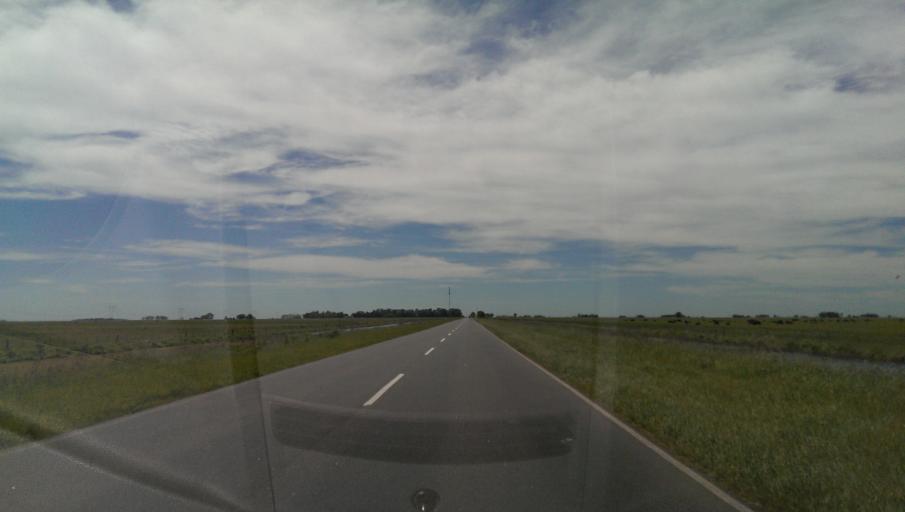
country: AR
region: Buenos Aires
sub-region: Partido de Laprida
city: Laprida
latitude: -37.2026
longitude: -60.6732
